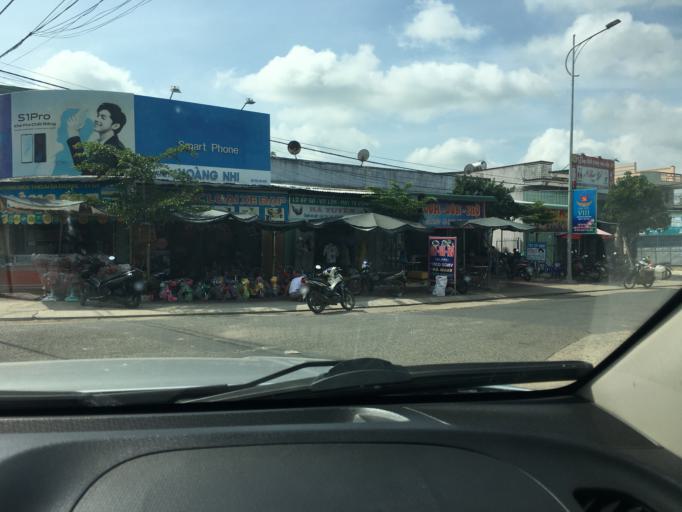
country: VN
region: Gia Lai
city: Kong Chro
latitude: 13.7771
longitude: 108.5243
